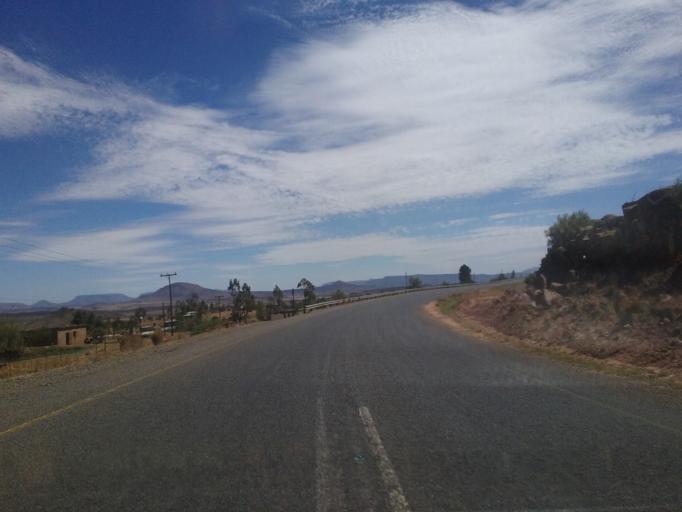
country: LS
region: Mohale's Hoek District
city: Mohale's Hoek
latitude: -30.1941
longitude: 27.4148
